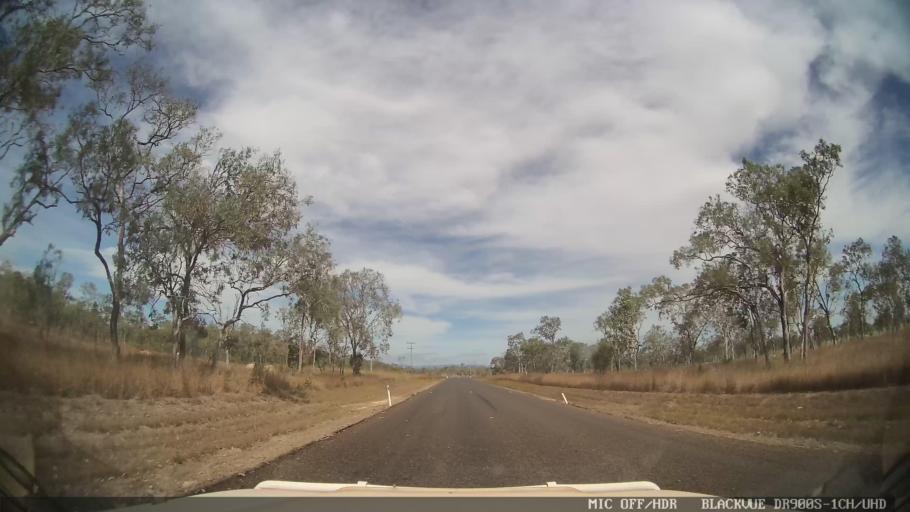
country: AU
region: Queensland
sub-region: Tablelands
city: Mareeba
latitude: -16.8476
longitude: 145.3809
